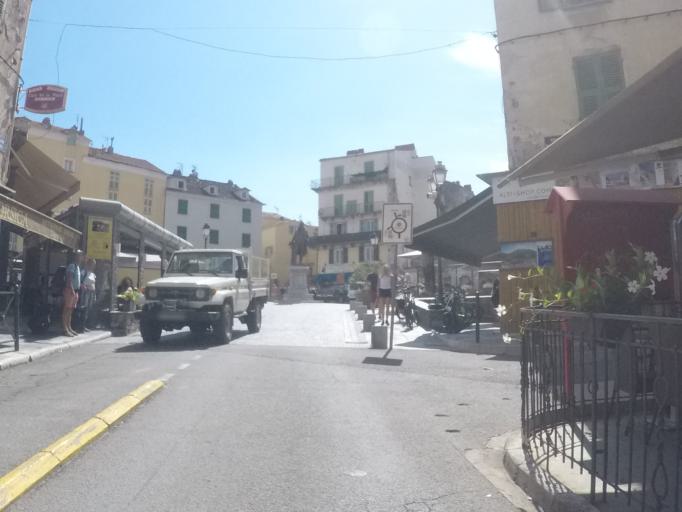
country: FR
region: Corsica
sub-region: Departement de la Haute-Corse
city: Corte
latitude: 42.3056
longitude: 9.1511
